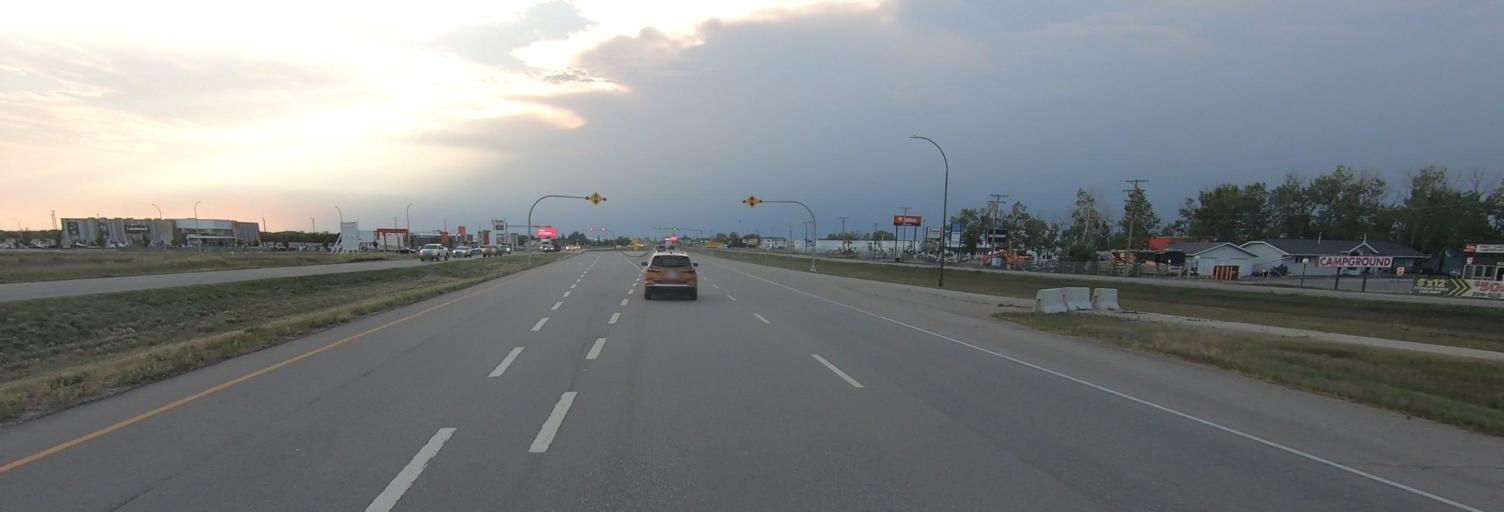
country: CA
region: Saskatchewan
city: Pilot Butte
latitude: 50.4478
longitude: -104.5081
